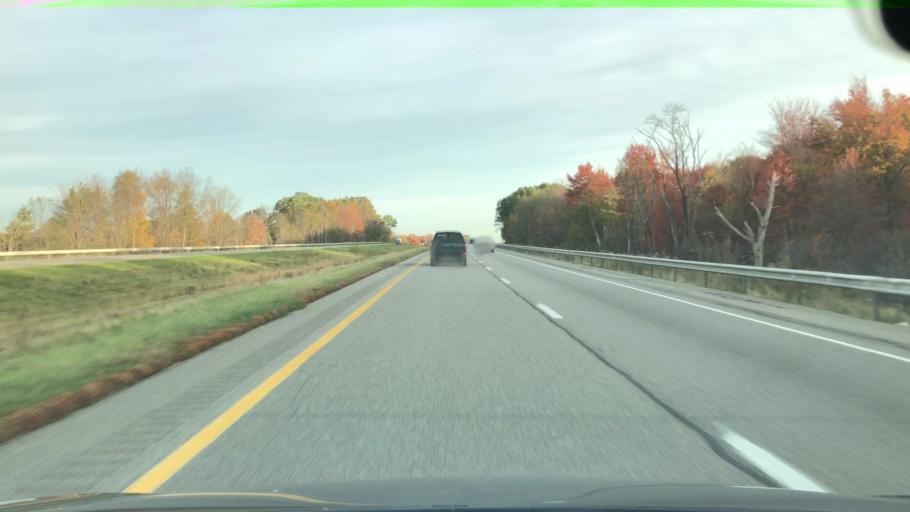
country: US
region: Pennsylvania
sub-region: Mercer County
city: Stoneboro
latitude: 41.3182
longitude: -80.1593
